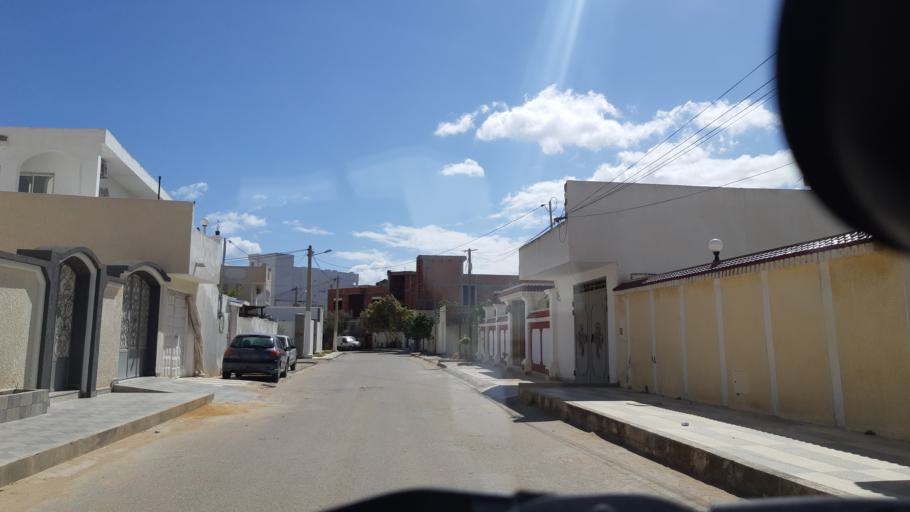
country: TN
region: Susah
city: Akouda
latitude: 35.8914
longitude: 10.5318
